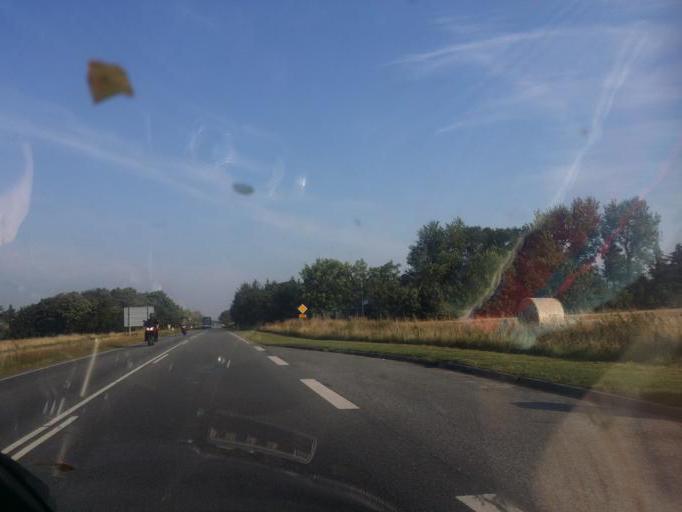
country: DK
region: South Denmark
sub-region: Tonder Kommune
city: Sherrebek
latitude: 55.1700
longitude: 8.7545
